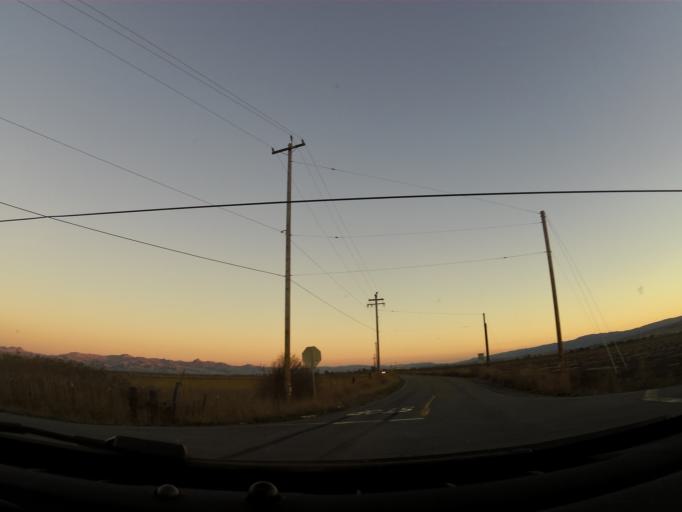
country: US
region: California
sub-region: Santa Clara County
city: Gilroy
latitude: 36.9785
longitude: -121.5085
